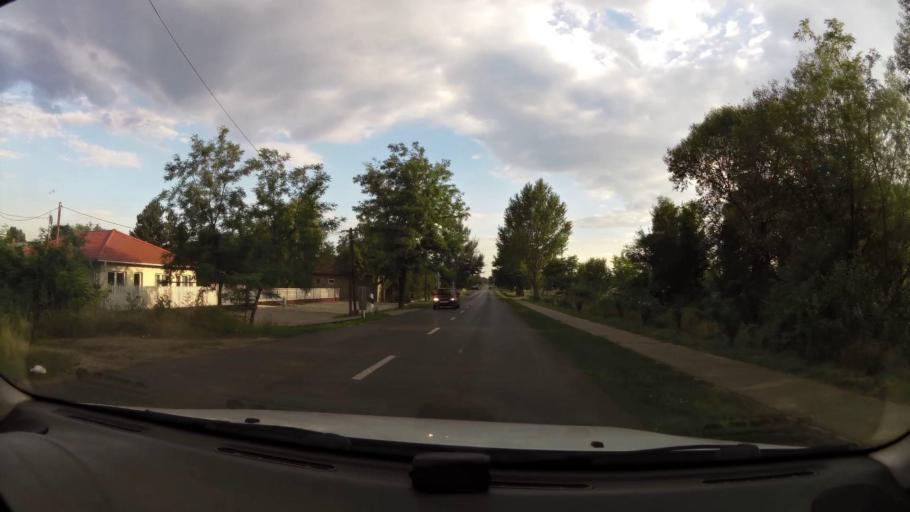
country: HU
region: Pest
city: Tapioszecso
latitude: 47.4440
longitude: 19.5990
